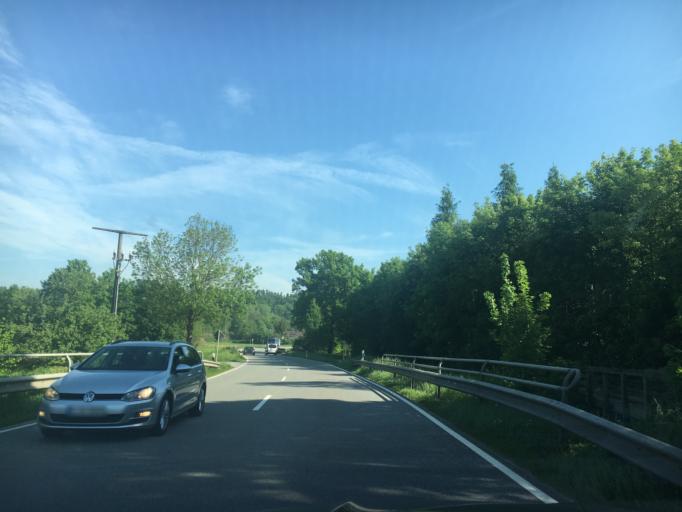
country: DE
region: Bavaria
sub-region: Upper Bavaria
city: Rohrbach
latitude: 48.2786
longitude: 12.5534
